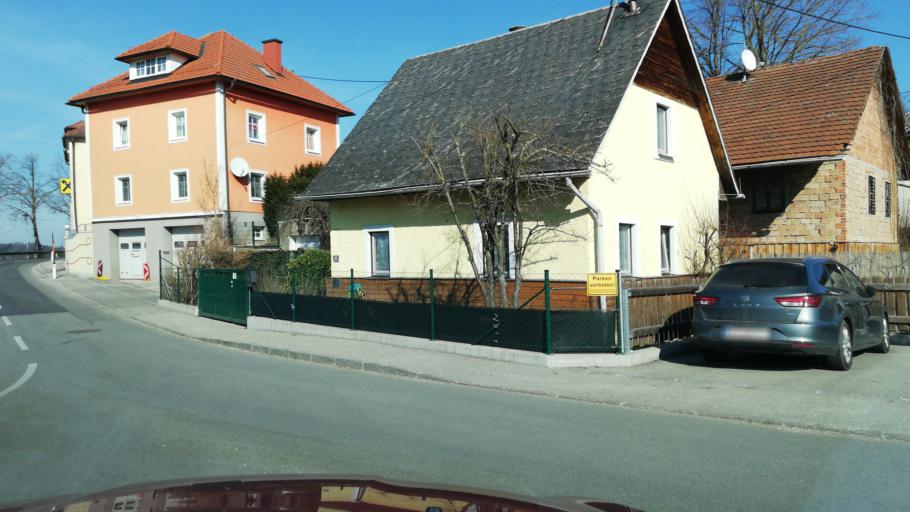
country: AT
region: Upper Austria
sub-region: Politischer Bezirk Vocklabruck
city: Rustorf
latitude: 48.0419
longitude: 13.7903
